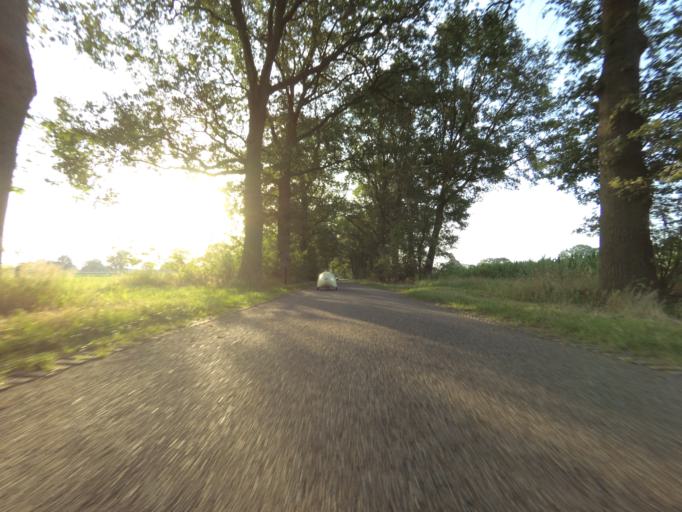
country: NL
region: Gelderland
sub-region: Gemeente Lochem
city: Laren
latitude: 52.2778
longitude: 6.3560
